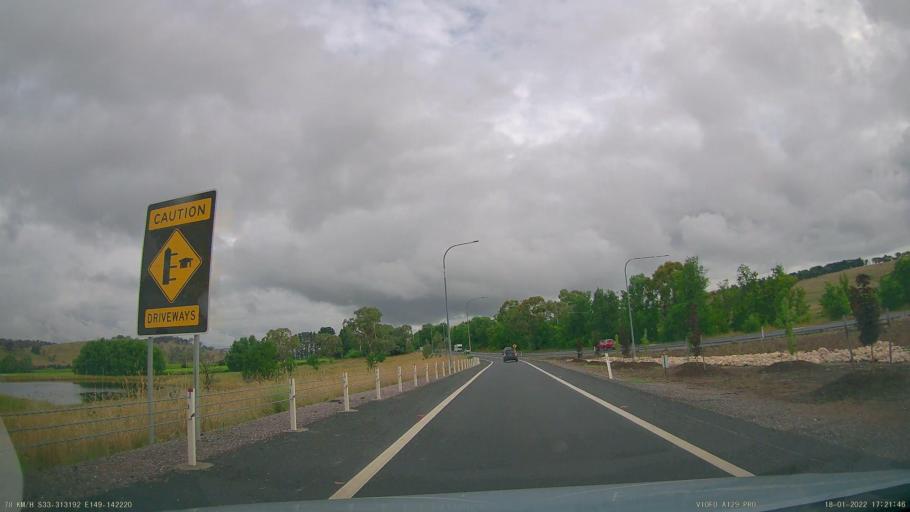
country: AU
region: New South Wales
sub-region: Orange Municipality
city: Orange
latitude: -33.3134
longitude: 149.1423
